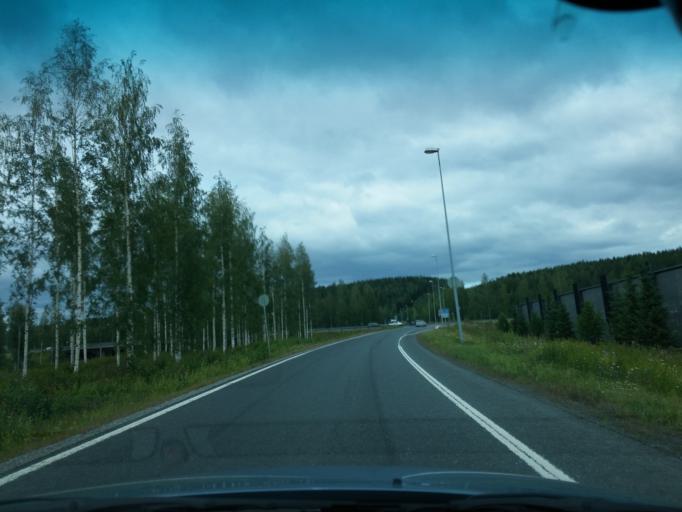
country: FI
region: Northern Savo
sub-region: Kuopio
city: Kuopio
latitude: 62.8390
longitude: 27.6072
